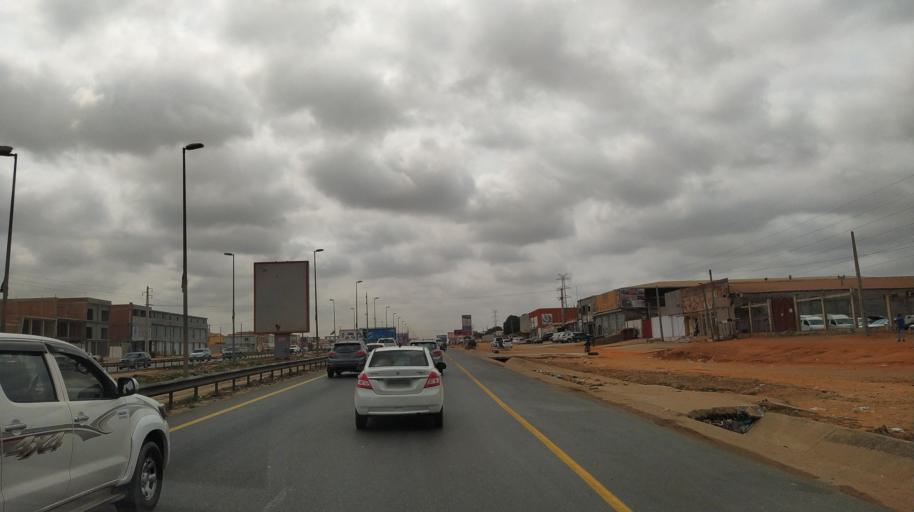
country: AO
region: Luanda
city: Luanda
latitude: -8.9730
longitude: 13.3072
